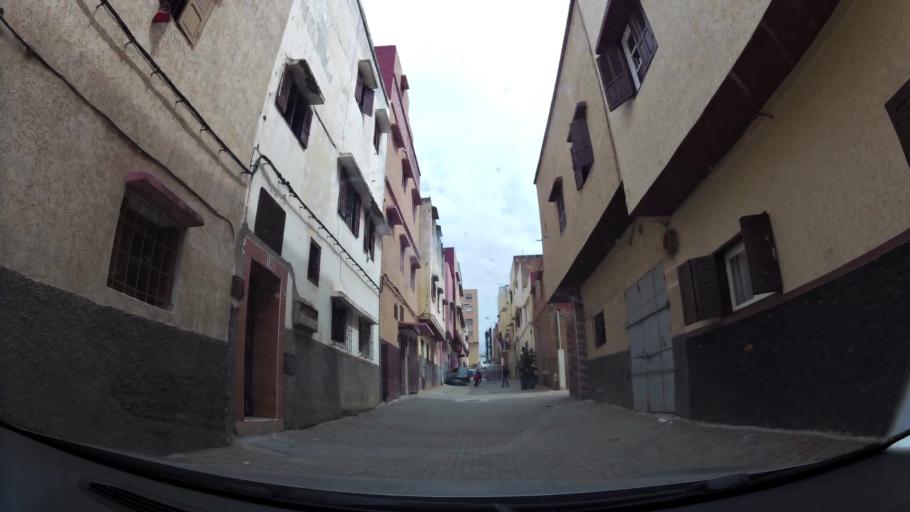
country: MA
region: Rabat-Sale-Zemmour-Zaer
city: Sale
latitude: 34.0341
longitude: -6.8041
